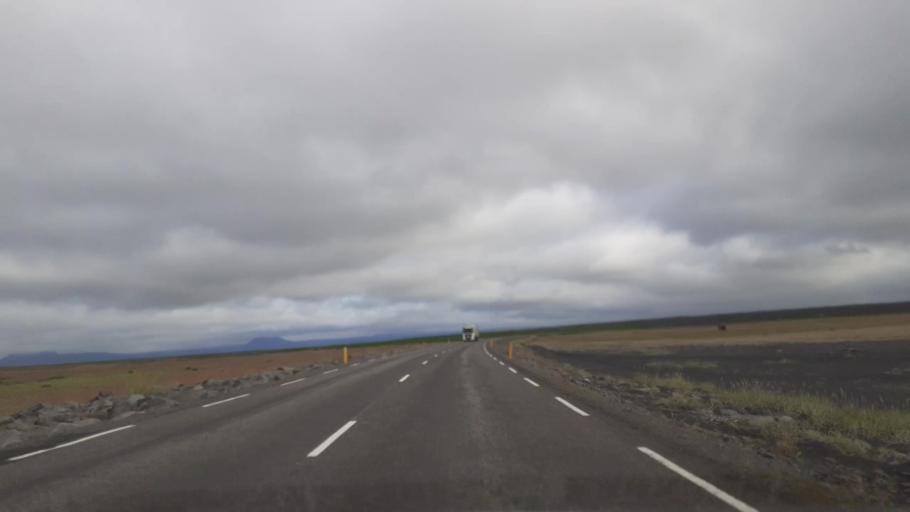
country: IS
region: Northeast
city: Husavik
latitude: 66.1192
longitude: -16.9228
